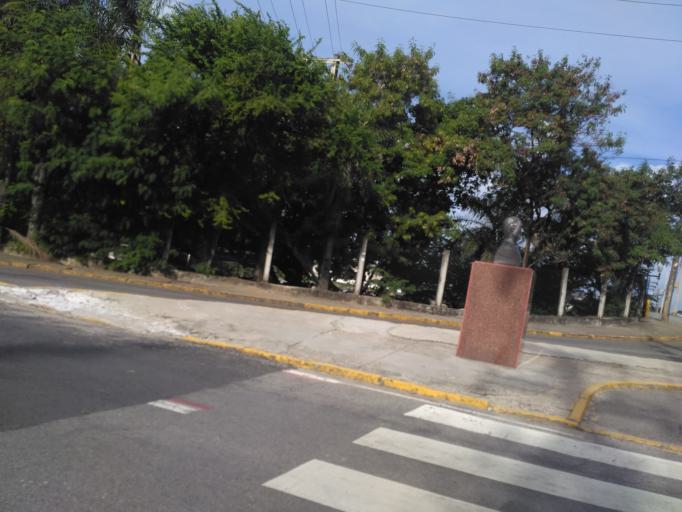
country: BR
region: Pernambuco
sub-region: Recife
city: Recife
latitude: -8.0499
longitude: -34.8738
